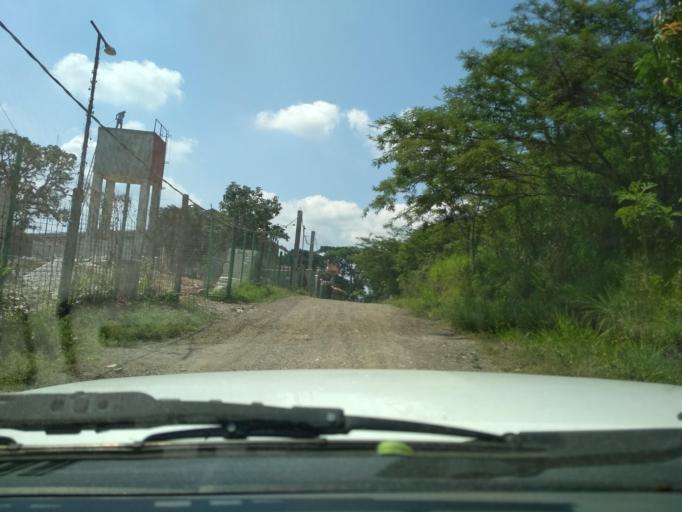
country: MX
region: Veracruz
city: Cordoba
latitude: 18.8760
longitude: -96.9124
